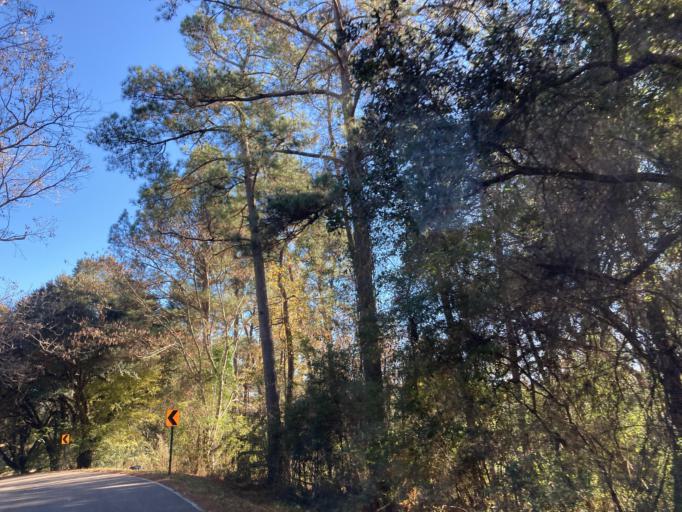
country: US
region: Mississippi
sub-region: Lamar County
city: Sumrall
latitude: 31.3683
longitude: -89.5786
